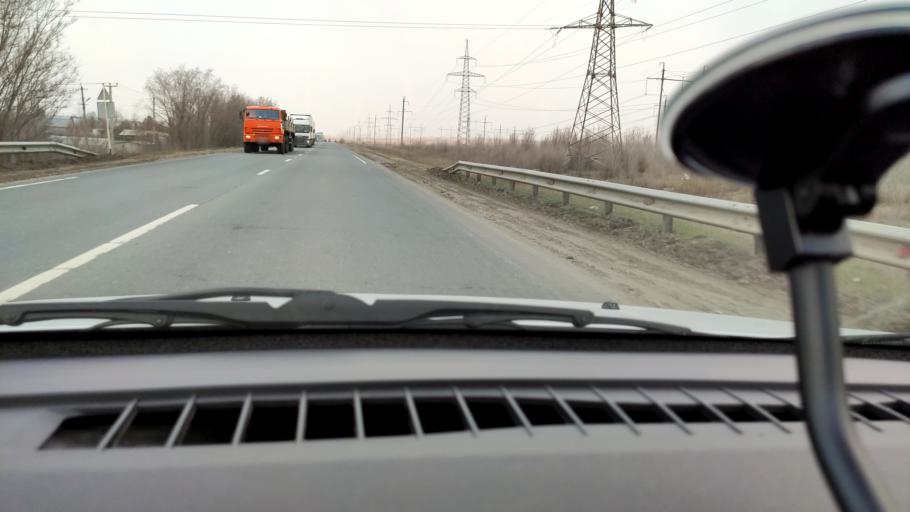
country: RU
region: Samara
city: Dubovyy Umet
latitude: 53.0836
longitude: 50.3920
